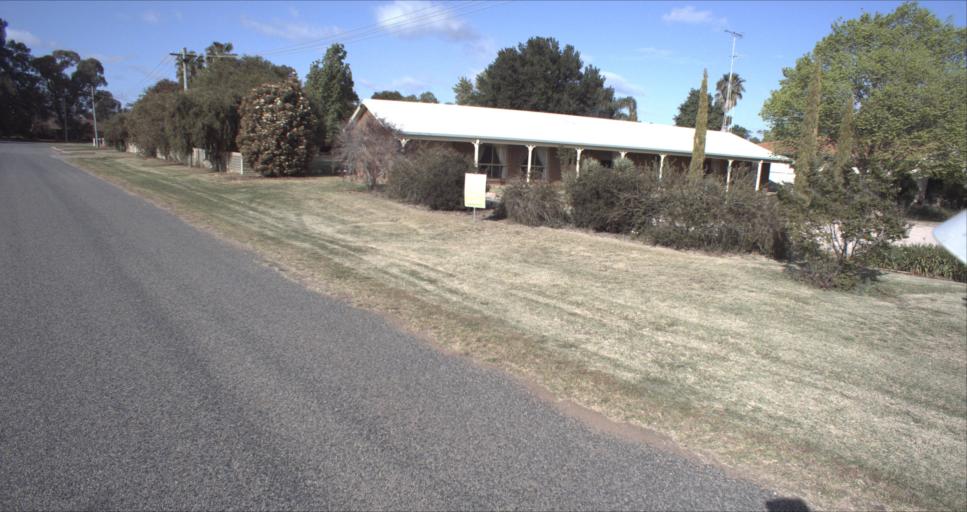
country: AU
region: New South Wales
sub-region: Leeton
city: Leeton
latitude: -34.5688
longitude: 146.3920
